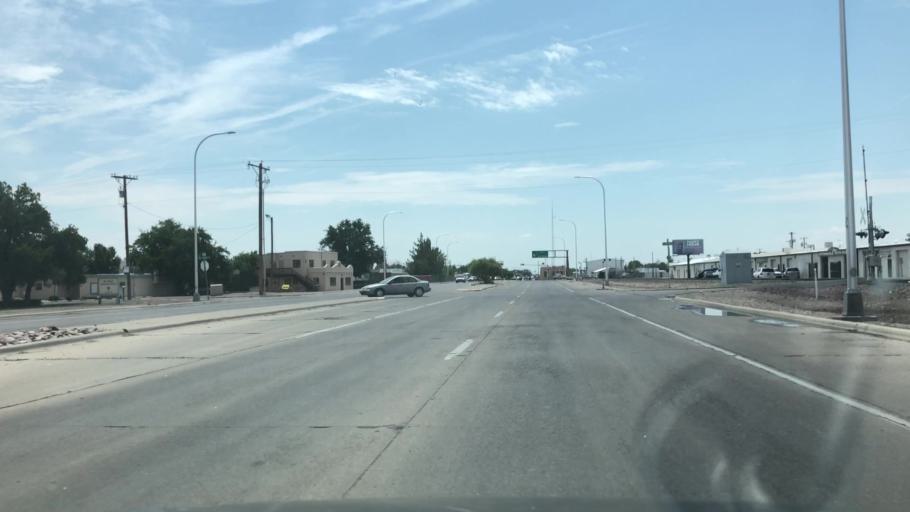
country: US
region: New Mexico
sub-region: Dona Ana County
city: University Park
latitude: 32.2799
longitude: -106.7695
